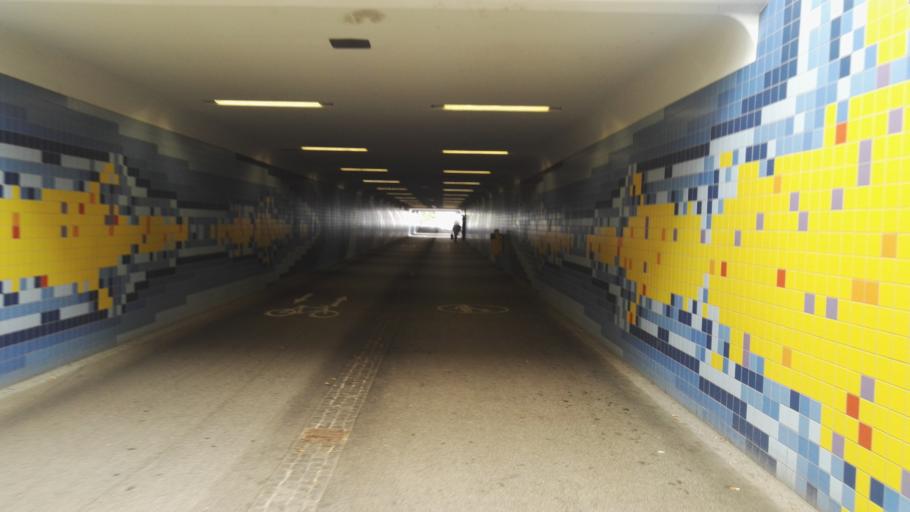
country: DE
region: Bavaria
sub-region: Upper Bavaria
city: Freilassing
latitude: 47.8373
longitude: 12.9788
